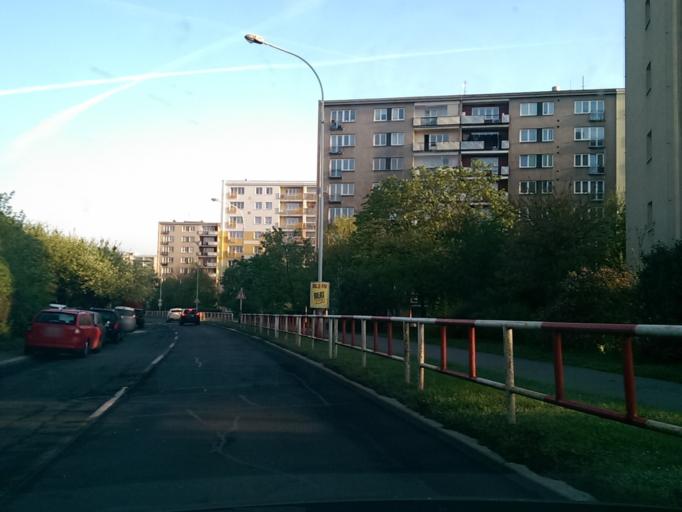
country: CZ
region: Praha
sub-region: Praha 8
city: Karlin
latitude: 50.0449
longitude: 14.4892
